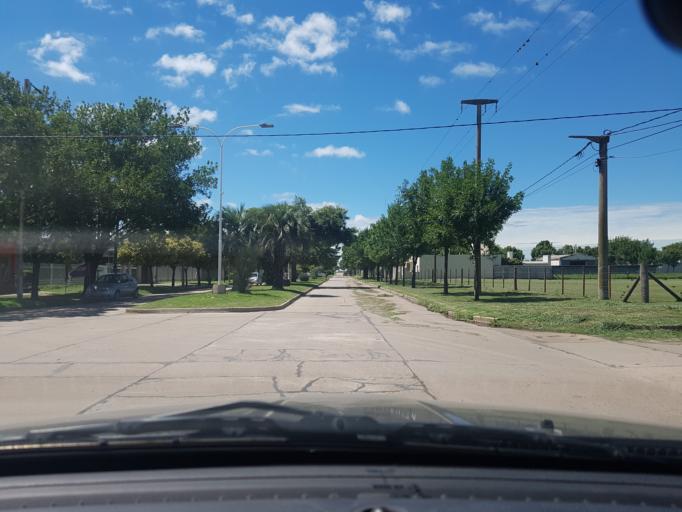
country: AR
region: Cordoba
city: General Cabrera
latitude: -32.7599
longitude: -63.7916
